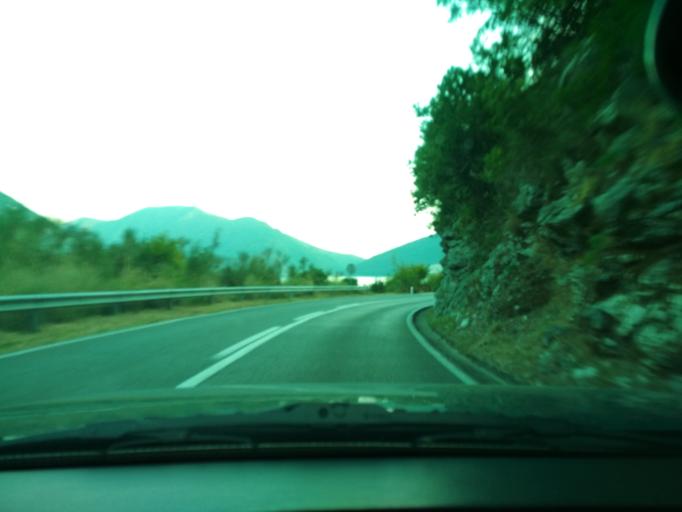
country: ME
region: Kotor
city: Risan
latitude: 42.5098
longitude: 18.6787
